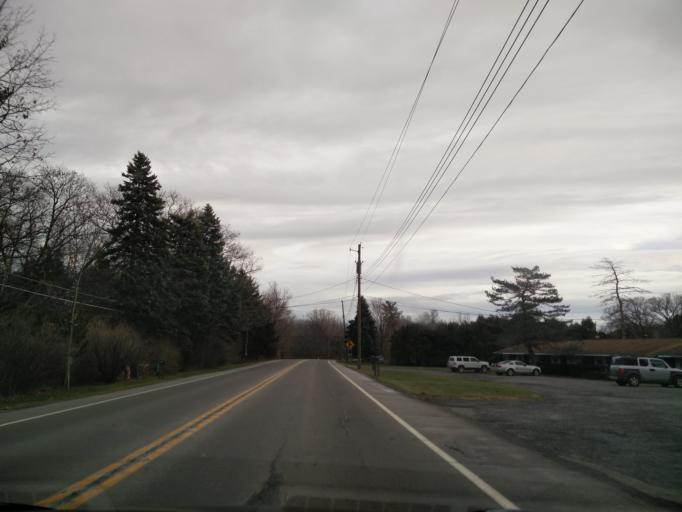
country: US
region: New York
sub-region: Tompkins County
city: Northwest Ithaca
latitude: 42.4817
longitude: -76.5636
